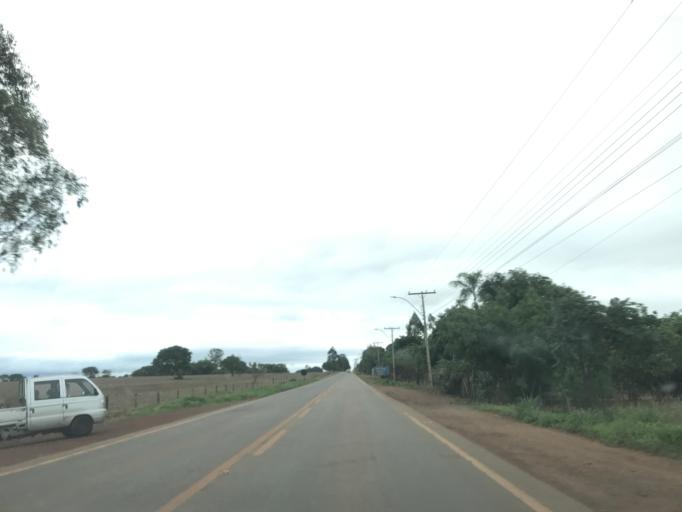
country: BR
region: Goias
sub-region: Luziania
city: Luziania
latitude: -16.3216
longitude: -48.0183
